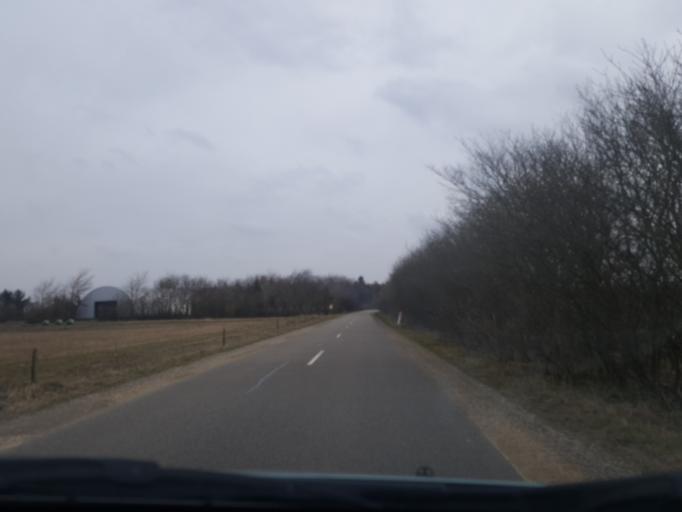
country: DK
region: Central Jutland
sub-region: Holstebro Kommune
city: Ulfborg
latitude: 56.1994
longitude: 8.2367
